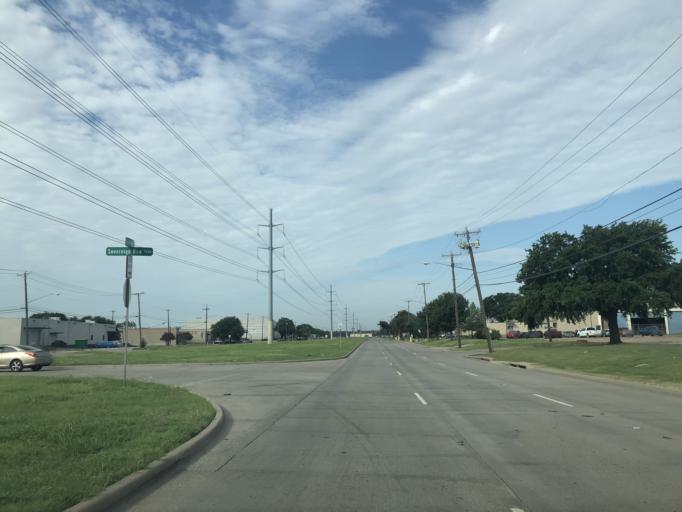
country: US
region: Texas
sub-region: Dallas County
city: Irving
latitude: 32.8237
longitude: -96.8910
